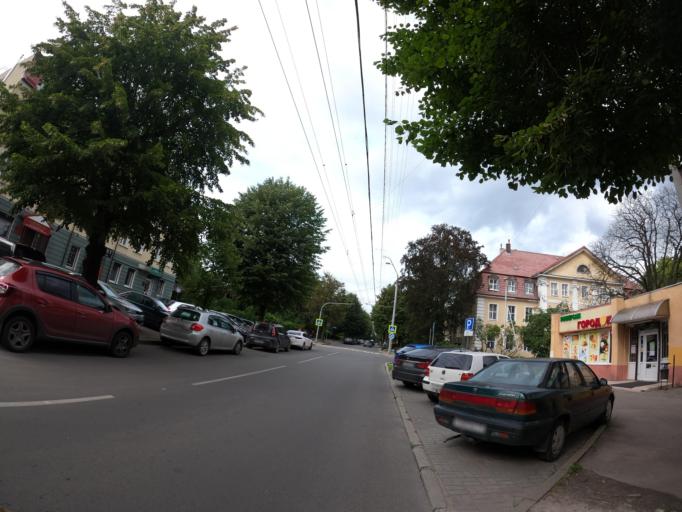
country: RU
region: Kaliningrad
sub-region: Gorod Kaliningrad
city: Kaliningrad
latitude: 54.7241
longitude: 20.4820
